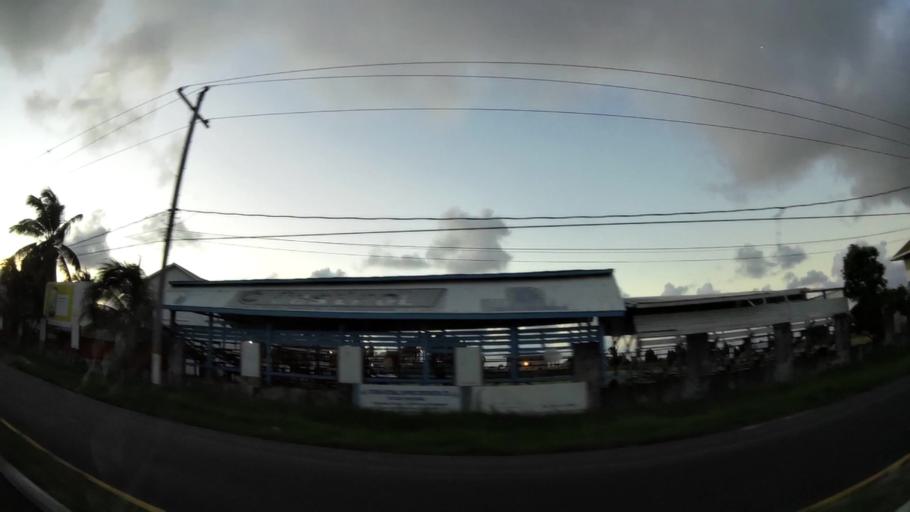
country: GY
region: Demerara-Mahaica
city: Georgetown
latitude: 6.8227
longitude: -58.1564
